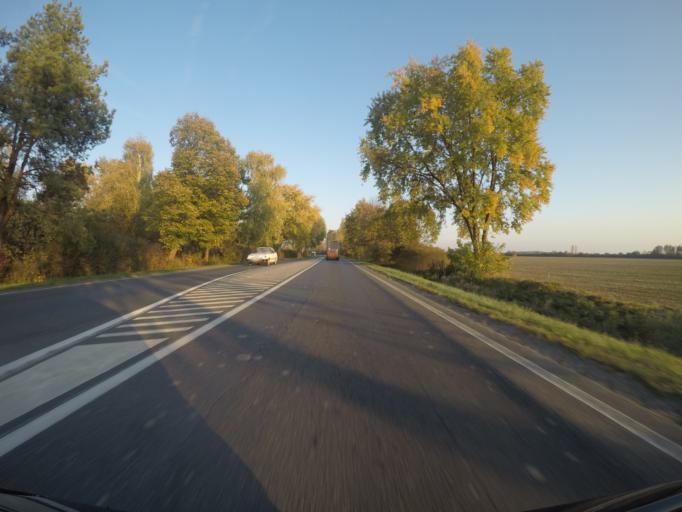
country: HU
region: Baranya
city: Szentlorinc
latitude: 46.0399
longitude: 17.9290
